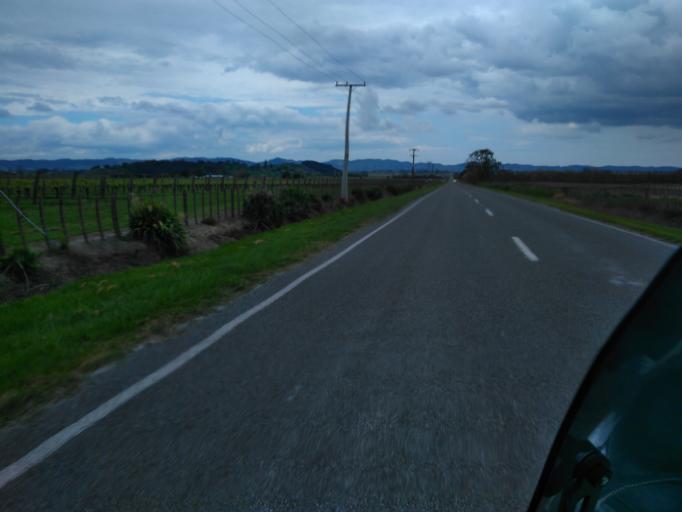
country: NZ
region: Gisborne
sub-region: Gisborne District
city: Gisborne
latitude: -38.6452
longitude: 177.8597
